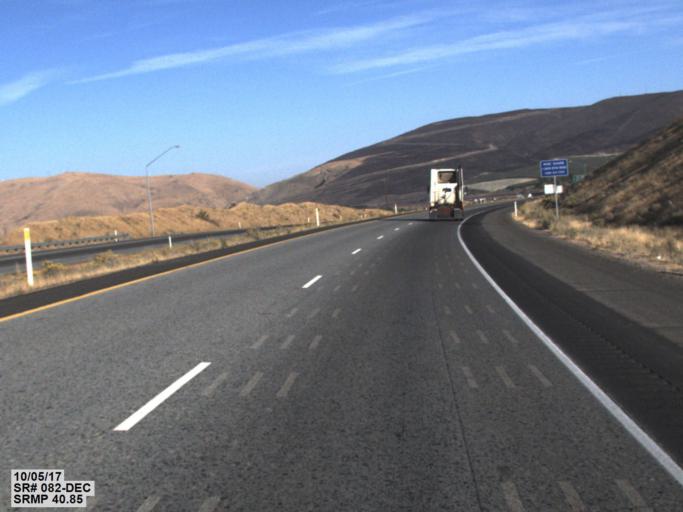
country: US
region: Washington
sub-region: Yakima County
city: Union Gap
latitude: 46.5043
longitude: -120.4493
